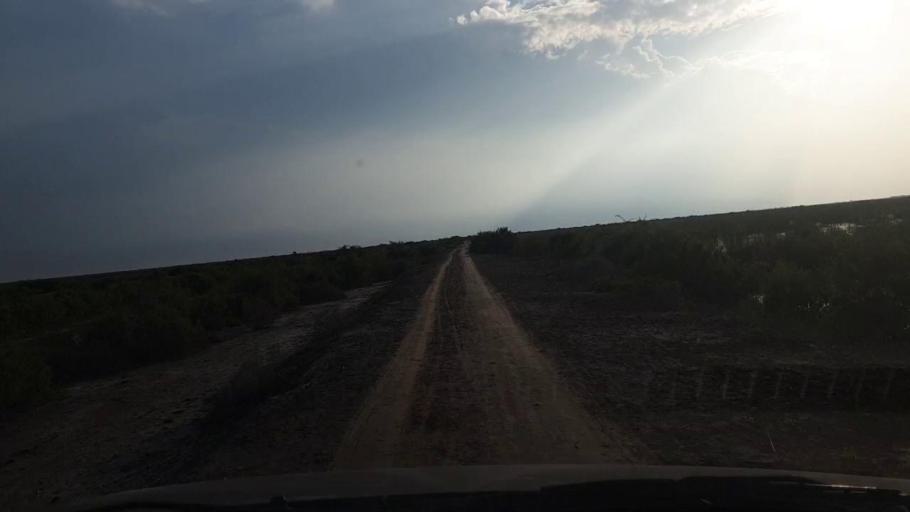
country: PK
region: Sindh
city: Badin
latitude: 24.4328
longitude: 68.6703
